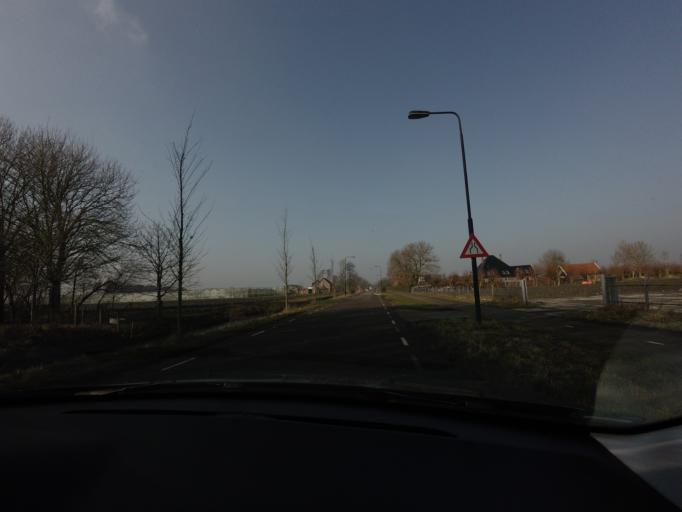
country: NL
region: North Holland
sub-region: Gemeente Heerhugowaard
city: Heerhugowaard
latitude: 52.6399
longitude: 4.8659
